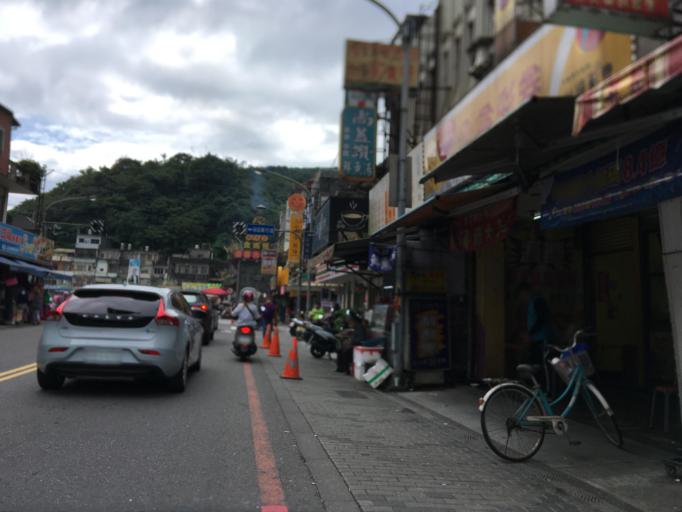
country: TW
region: Taiwan
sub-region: Yilan
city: Yilan
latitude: 24.5825
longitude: 121.8649
